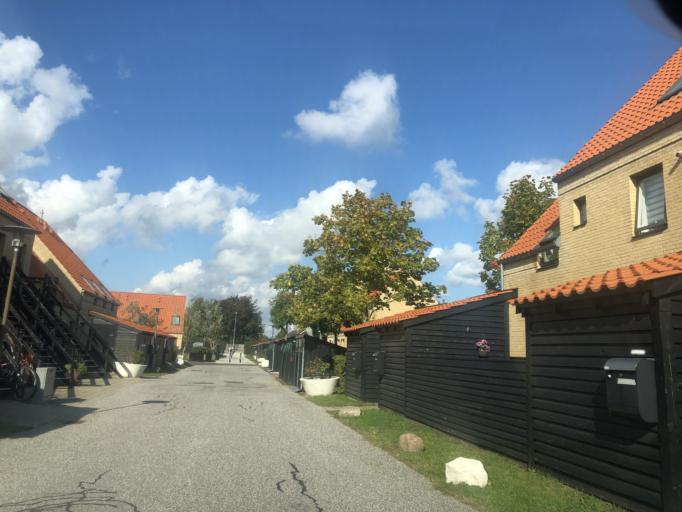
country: DK
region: Capital Region
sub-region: Tarnby Kommune
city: Tarnby
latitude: 55.6088
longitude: 12.5942
